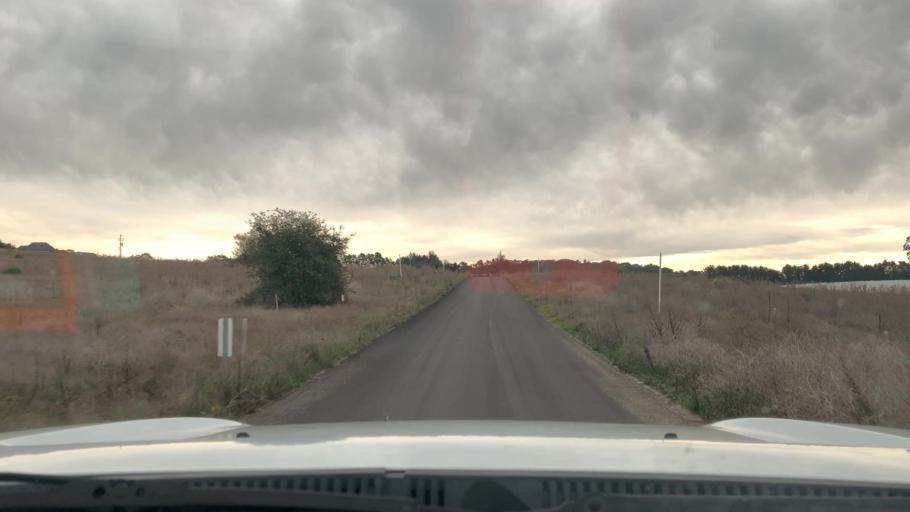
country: US
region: California
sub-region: San Luis Obispo County
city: Callender
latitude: 35.0659
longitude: -120.5667
